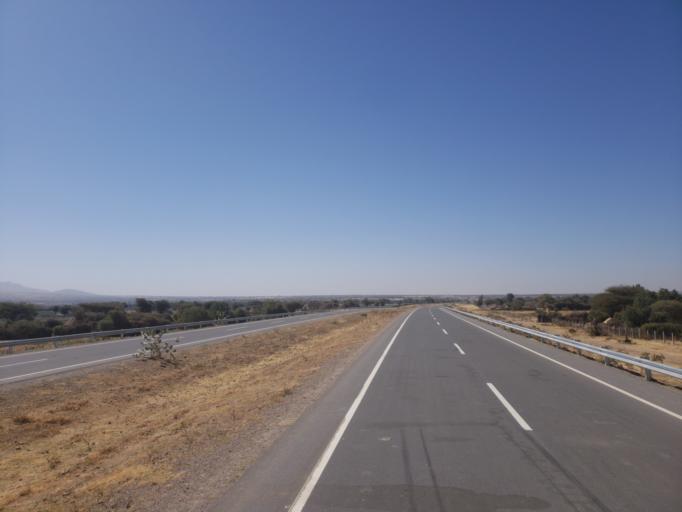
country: ET
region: Oromiya
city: Mojo
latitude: 8.3527
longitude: 38.9843
